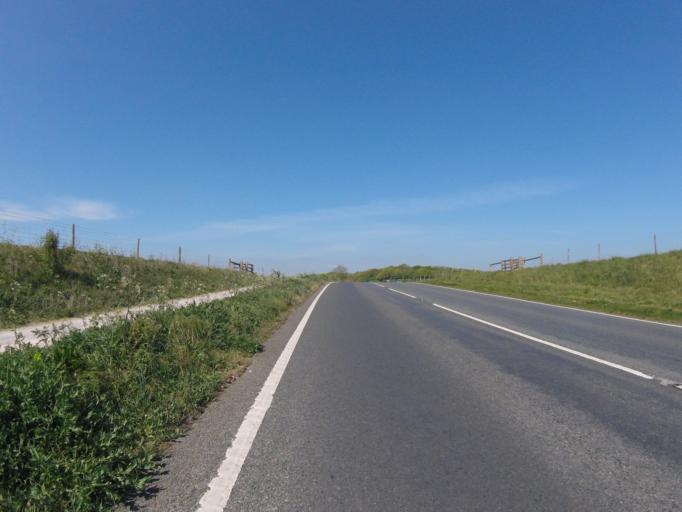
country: GB
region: England
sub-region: Brighton and Hove
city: Brighton
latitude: 50.8650
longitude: -0.1206
